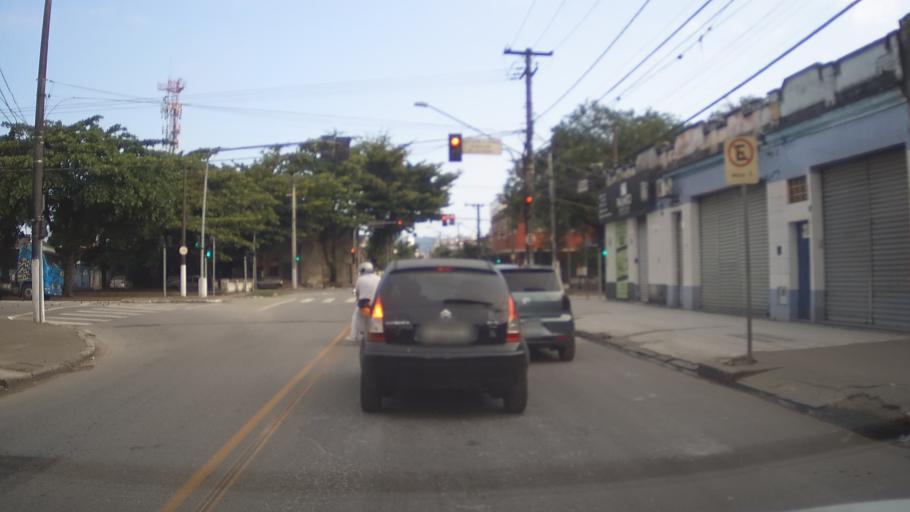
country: BR
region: Sao Paulo
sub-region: Santos
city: Santos
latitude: -23.9602
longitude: -46.3090
